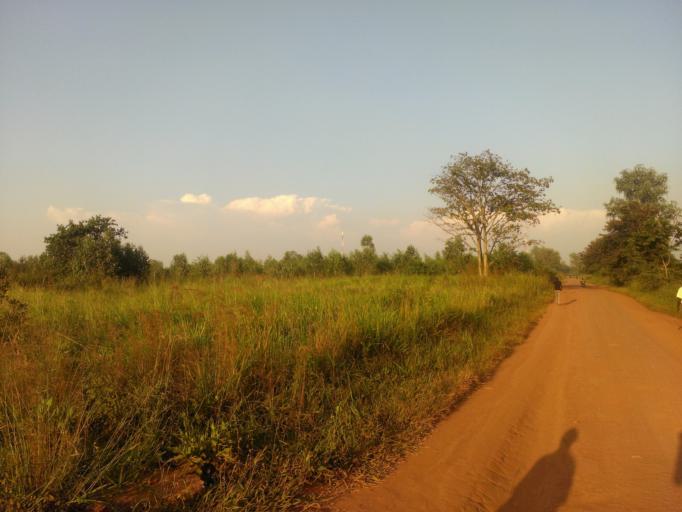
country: UG
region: Northern Region
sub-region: Gulu District
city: Gulu
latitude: 2.7819
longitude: 32.3102
